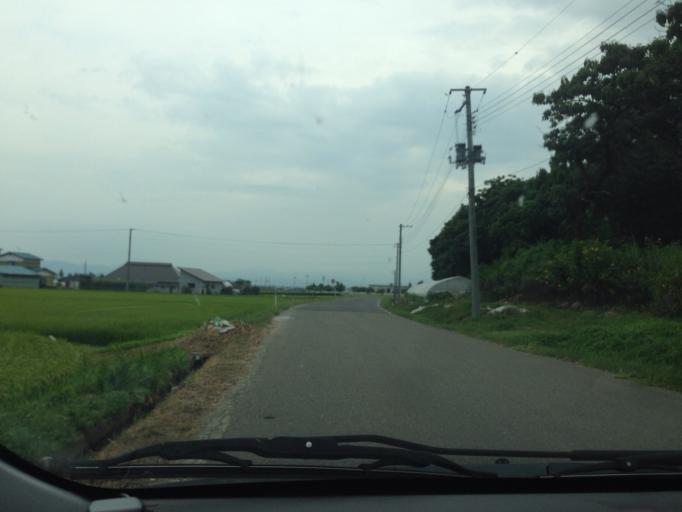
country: JP
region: Fukushima
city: Kitakata
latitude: 37.6512
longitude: 139.8454
